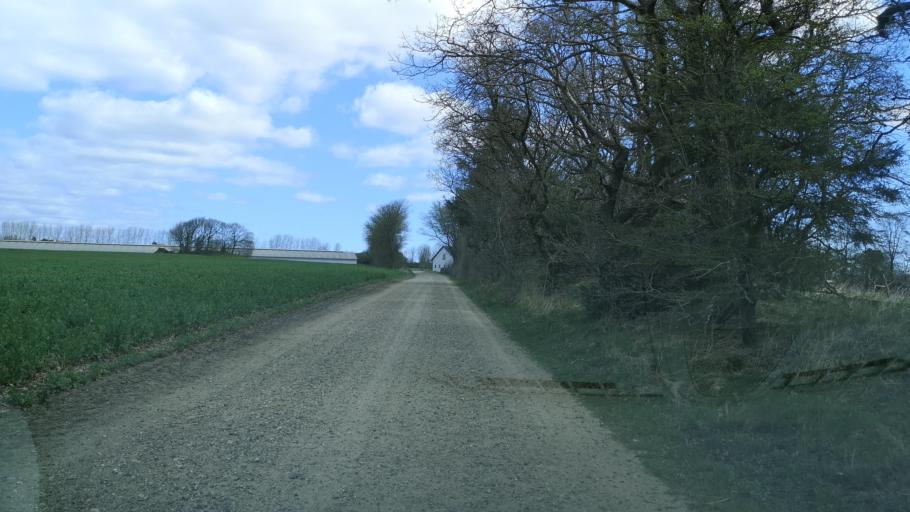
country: DK
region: Central Jutland
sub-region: Ringkobing-Skjern Kommune
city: Skjern
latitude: 55.9711
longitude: 8.5010
